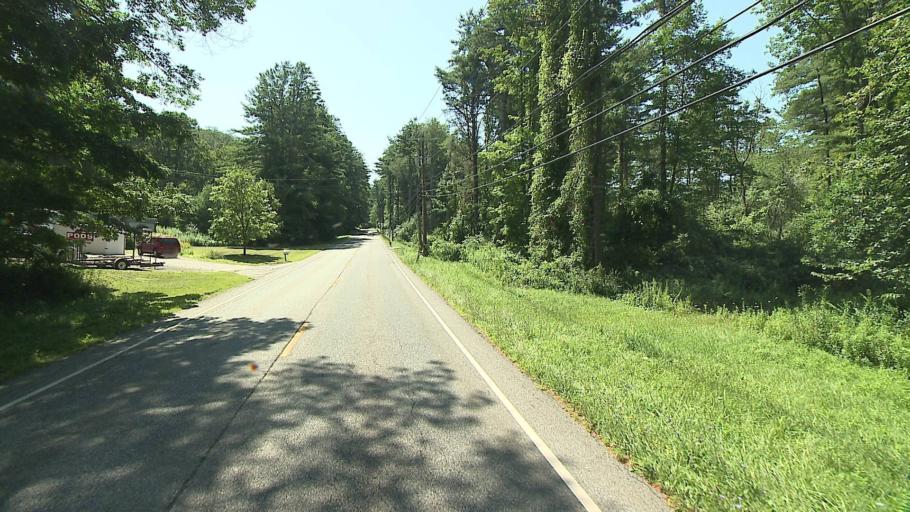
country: US
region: Connecticut
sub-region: Litchfield County
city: Kent
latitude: 41.8639
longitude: -73.4633
